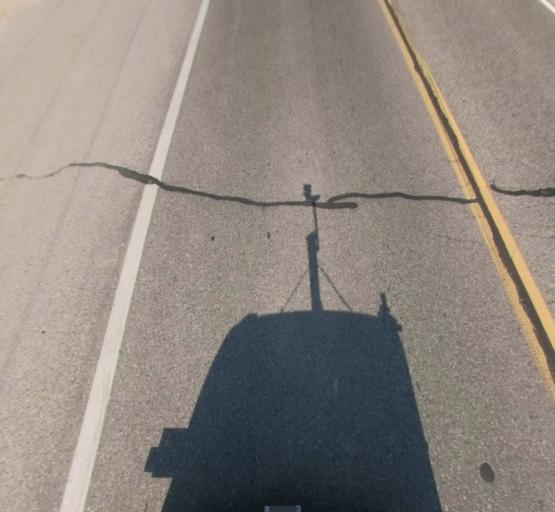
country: US
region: California
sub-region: Madera County
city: Yosemite Lakes
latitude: 37.2062
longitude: -119.7761
